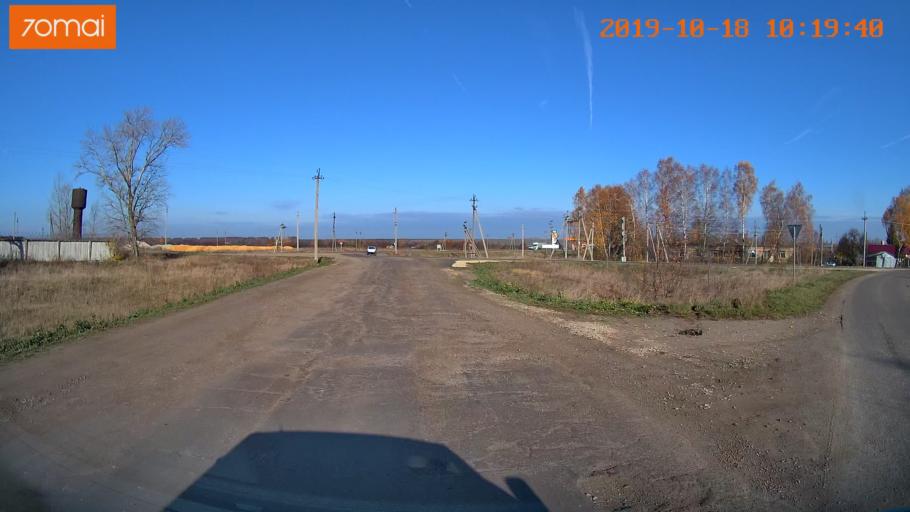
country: RU
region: Tula
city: Kurkino
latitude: 53.4238
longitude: 38.6452
